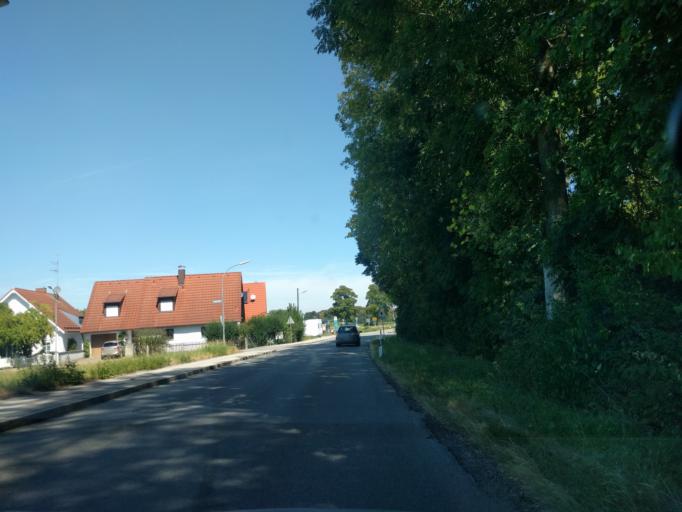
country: DE
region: Bavaria
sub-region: Upper Bavaria
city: Fuerstenfeldbruck
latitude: 48.1879
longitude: 11.2257
